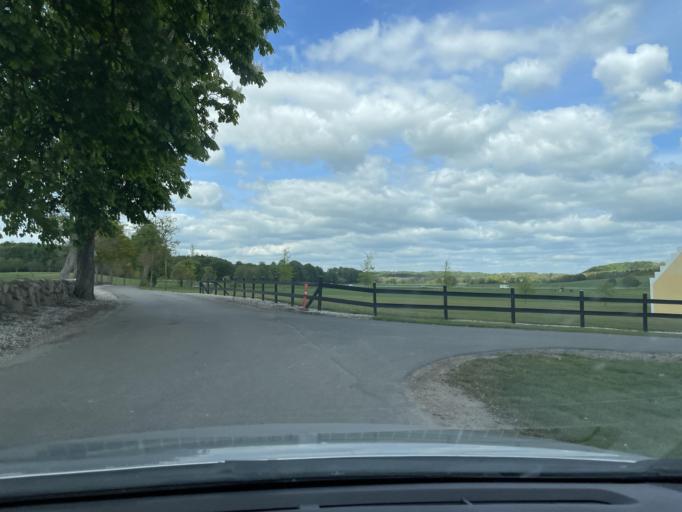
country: DK
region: Central Jutland
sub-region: Odder Kommune
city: Odder
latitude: 55.9118
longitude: 10.1013
